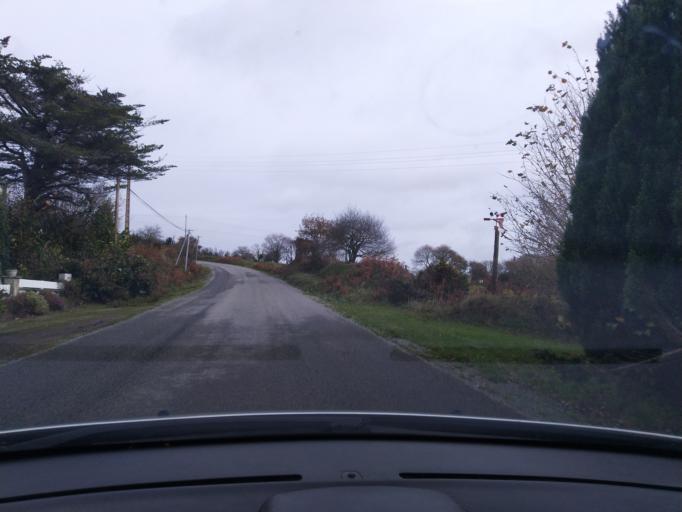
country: FR
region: Brittany
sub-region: Departement du Finistere
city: Guerlesquin
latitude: 48.5251
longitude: -3.5721
